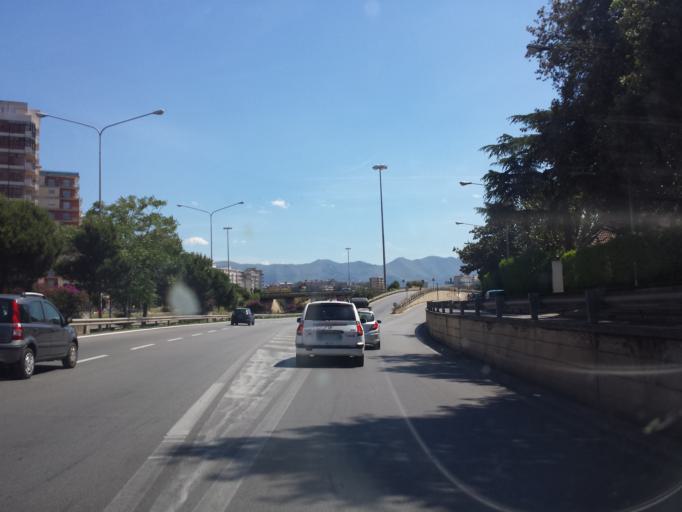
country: IT
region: Sicily
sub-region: Palermo
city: Palermo
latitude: 38.1425
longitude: 13.3312
